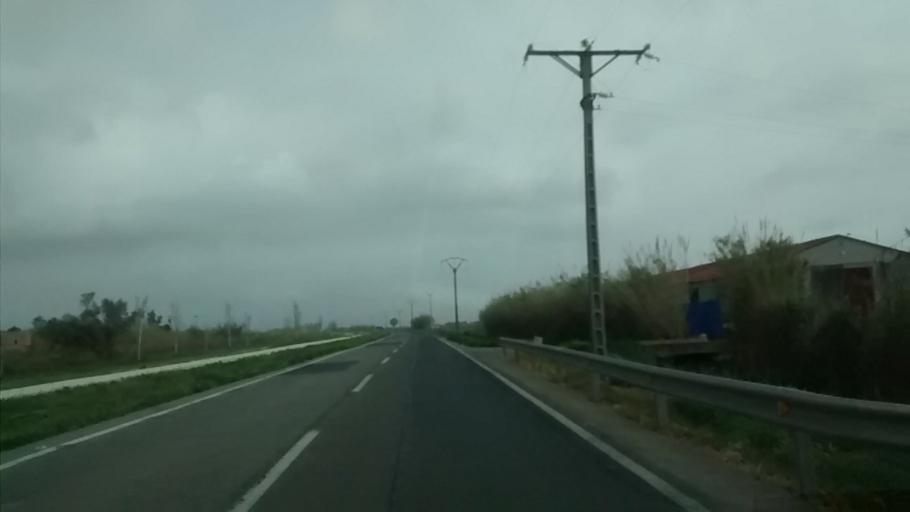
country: ES
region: Catalonia
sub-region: Provincia de Tarragona
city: Sant Carles de la Rapita
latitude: 40.6298
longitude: 0.6009
